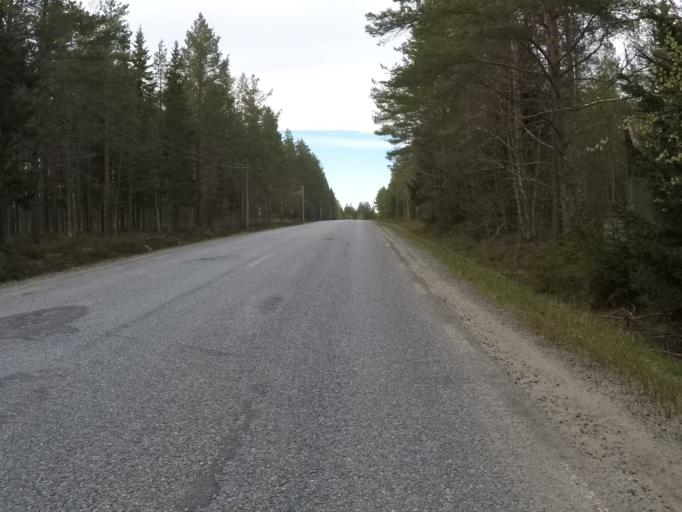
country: SE
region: Vaesterbotten
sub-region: Umea Kommun
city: Saevar
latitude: 63.9343
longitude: 20.7822
